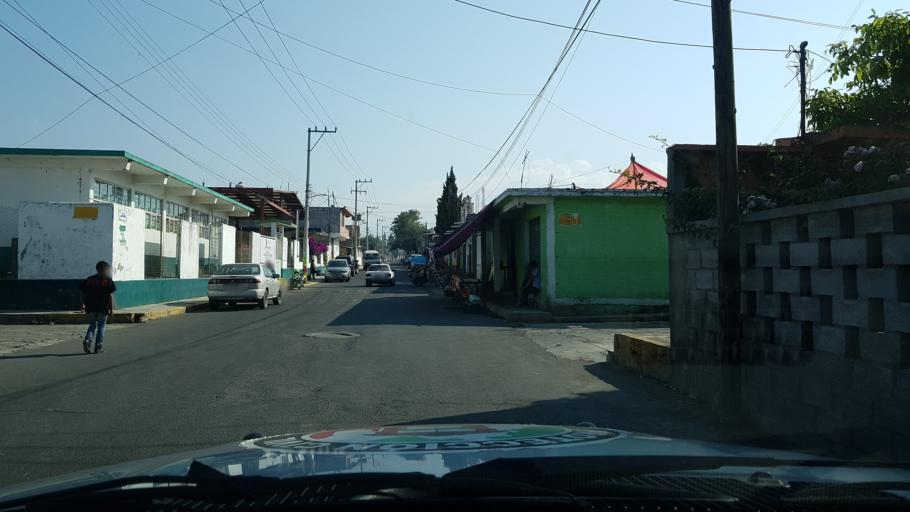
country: MX
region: Mexico
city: Atlautla
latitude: 19.0338
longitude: -98.7774
